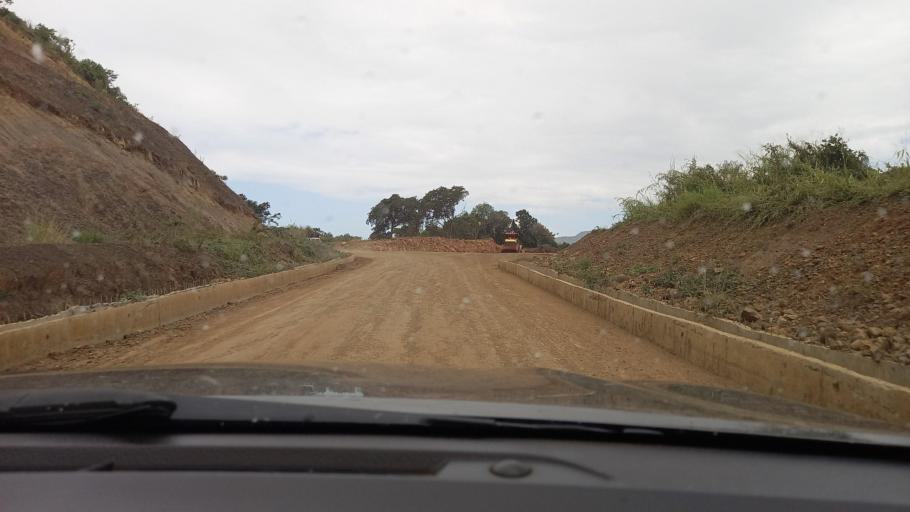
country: ET
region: Southern Nations, Nationalities, and People's Region
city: Mizan Teferi
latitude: 6.2017
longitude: 35.6755
